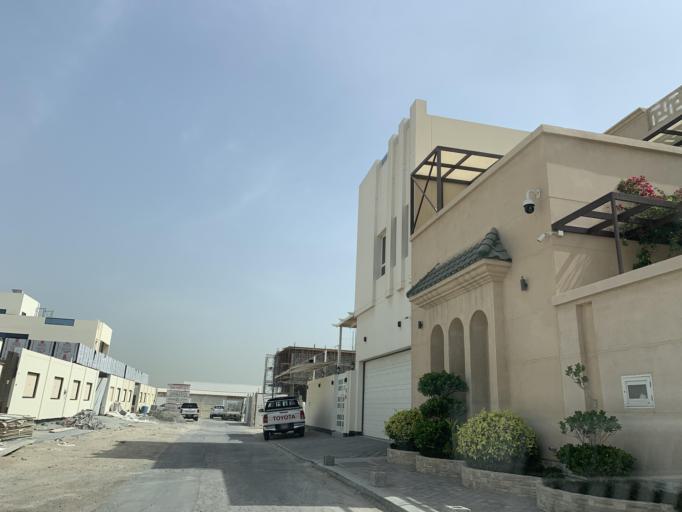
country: BH
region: Northern
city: Madinat `Isa
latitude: 26.1746
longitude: 50.5711
